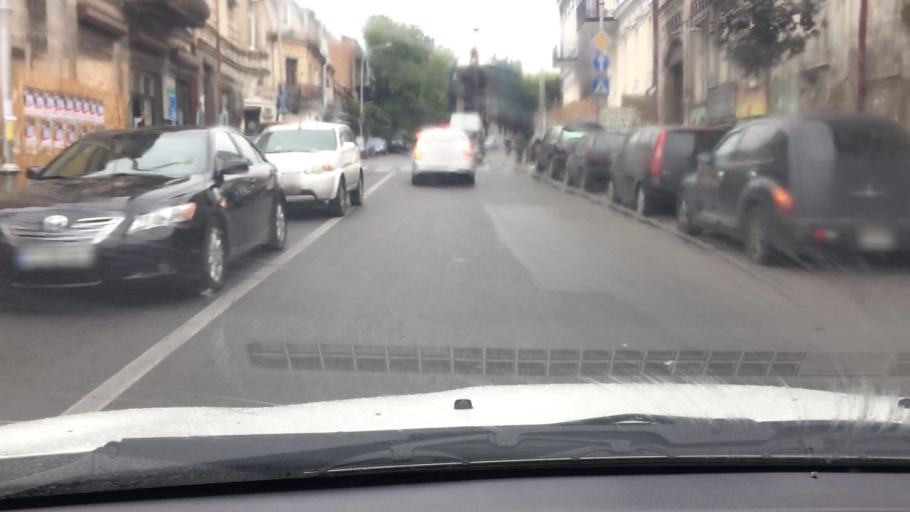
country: GE
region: T'bilisi
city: Tbilisi
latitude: 41.7035
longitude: 44.8062
